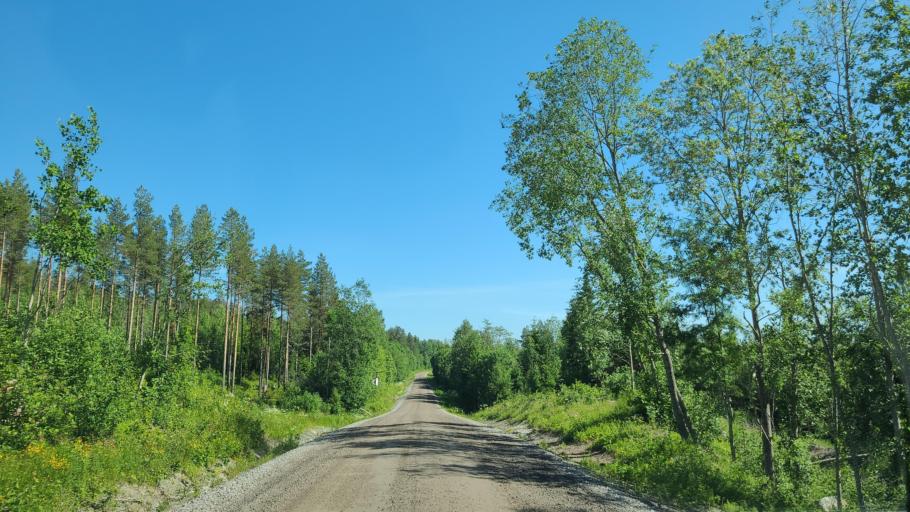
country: SE
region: Vaesterbotten
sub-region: Bjurholms Kommun
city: Bjurholm
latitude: 63.6797
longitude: 18.9954
